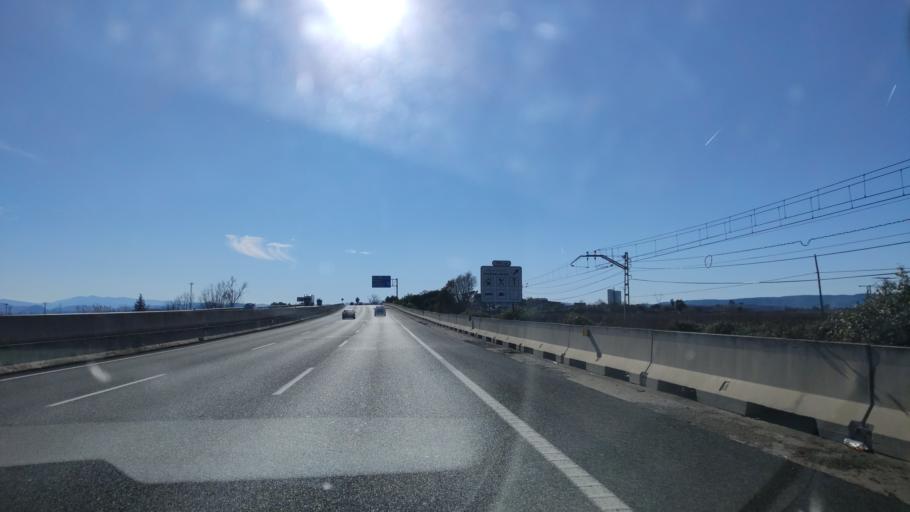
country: ES
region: Valencia
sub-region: Provincia de Valencia
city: L'Alcudia
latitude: 39.1789
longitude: -0.5147
